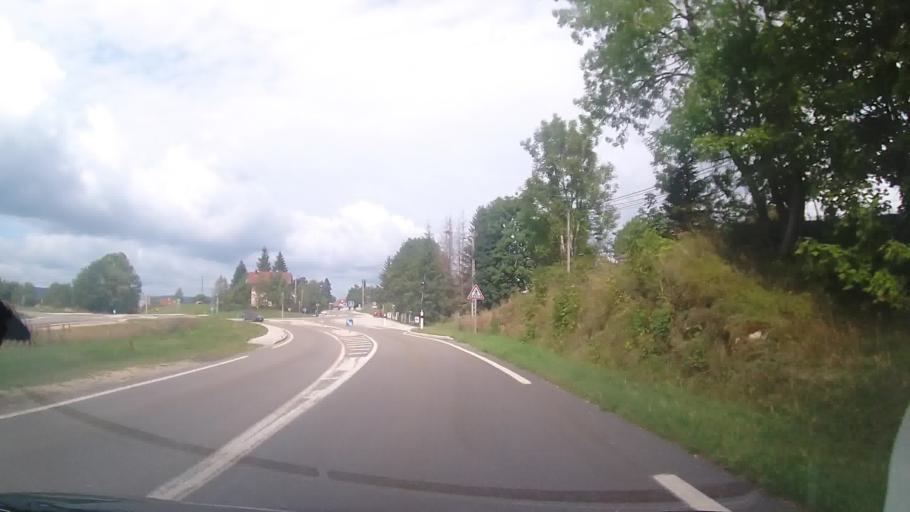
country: FR
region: Franche-Comte
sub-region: Departement du Jura
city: Les Rousses
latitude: 46.4617
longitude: 6.0721
